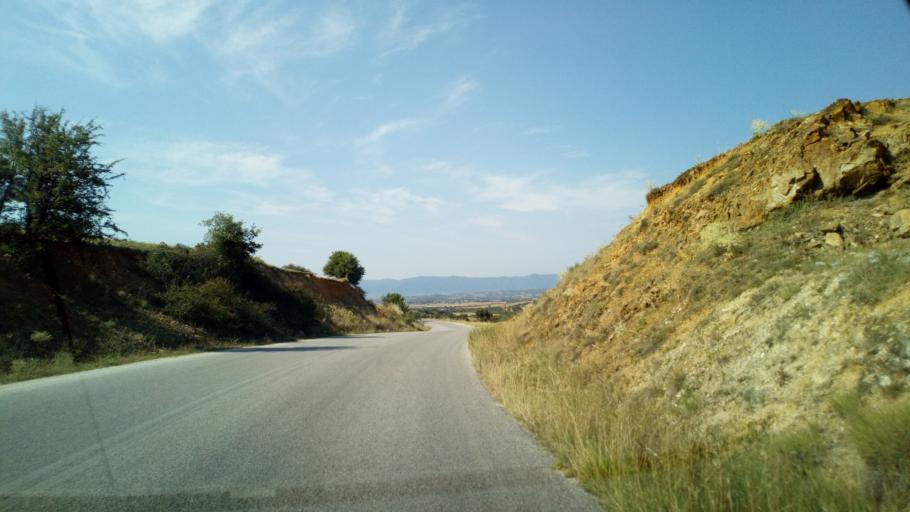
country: GR
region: Central Macedonia
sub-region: Nomos Thessalonikis
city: Nea Apollonia
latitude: 40.5177
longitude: 23.4728
